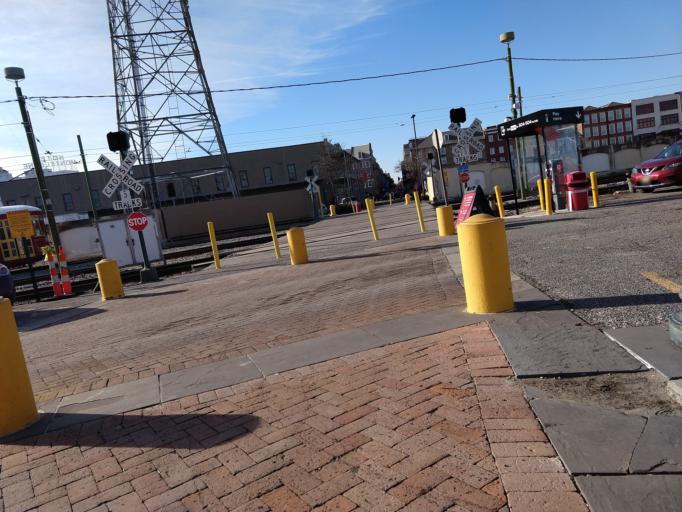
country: US
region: Louisiana
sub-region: Orleans Parish
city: New Orleans
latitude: 29.9544
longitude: -90.0631
